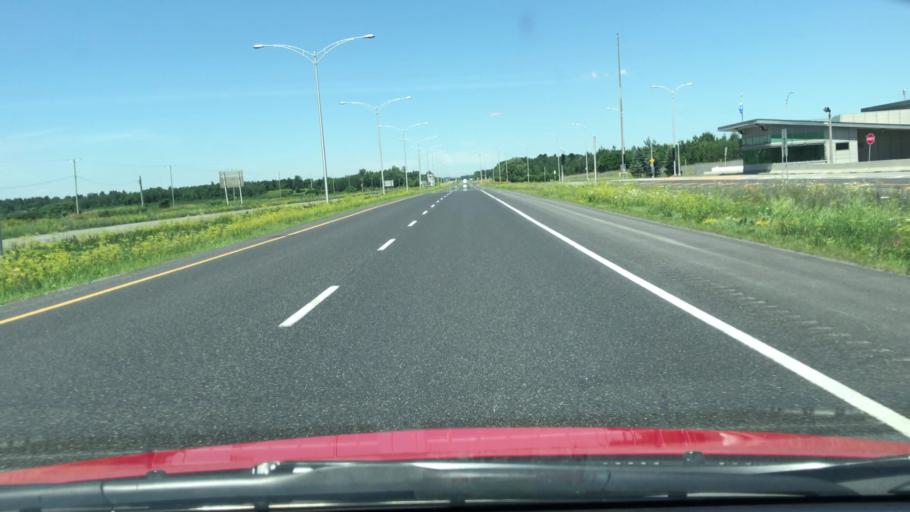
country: US
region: New York
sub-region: Clinton County
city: Champlain
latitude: 45.0353
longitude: -73.4534
